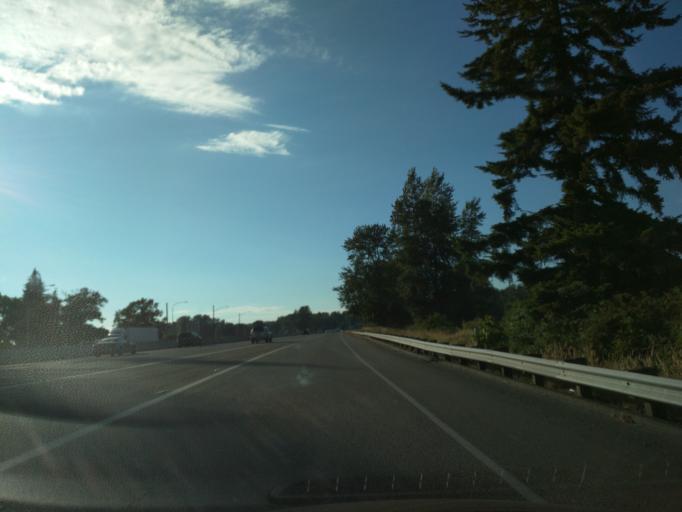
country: US
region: Washington
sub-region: Snohomish County
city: Smokey Point
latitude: 48.1896
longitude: -122.2041
